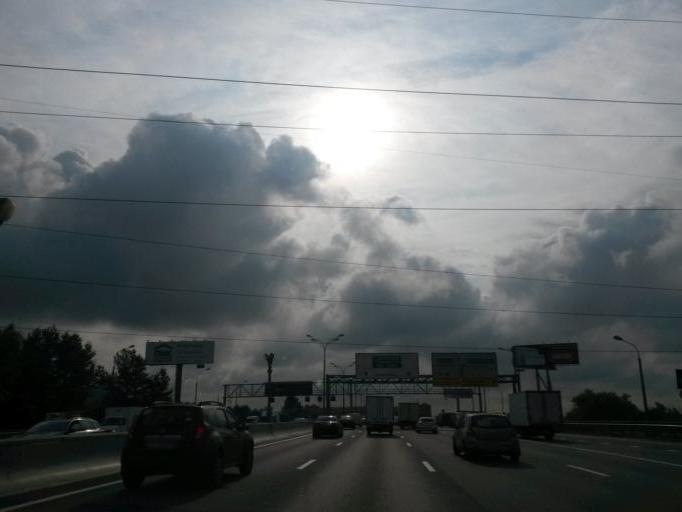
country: RU
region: Moskovskaya
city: Biryulevo Zapadnoye
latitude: 55.5732
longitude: 37.6436
